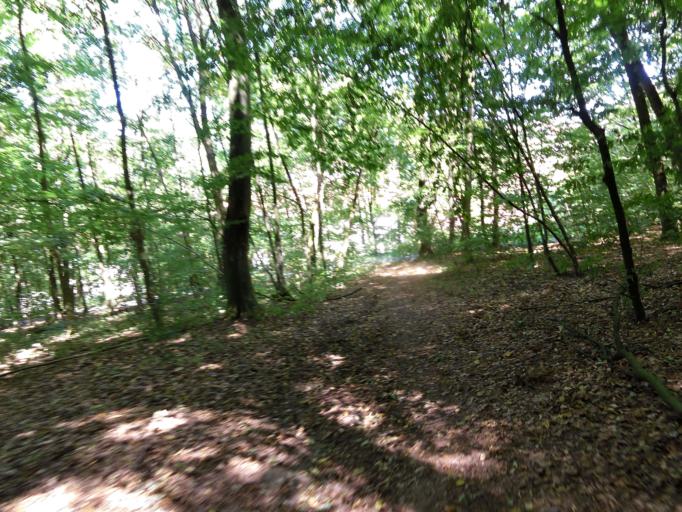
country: DE
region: Bavaria
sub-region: Regierungsbezirk Unterfranken
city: Theilheim
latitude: 49.7518
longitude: 10.0171
